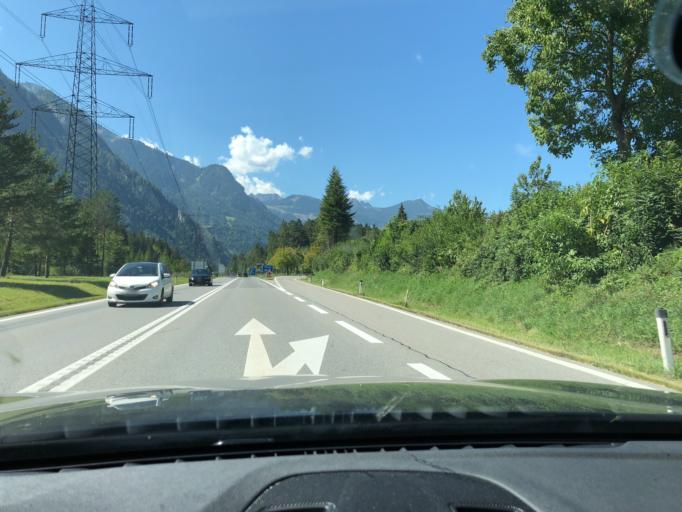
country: AT
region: Vorarlberg
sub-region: Politischer Bezirk Bludenz
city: Stallehr
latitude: 47.1415
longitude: 9.8533
